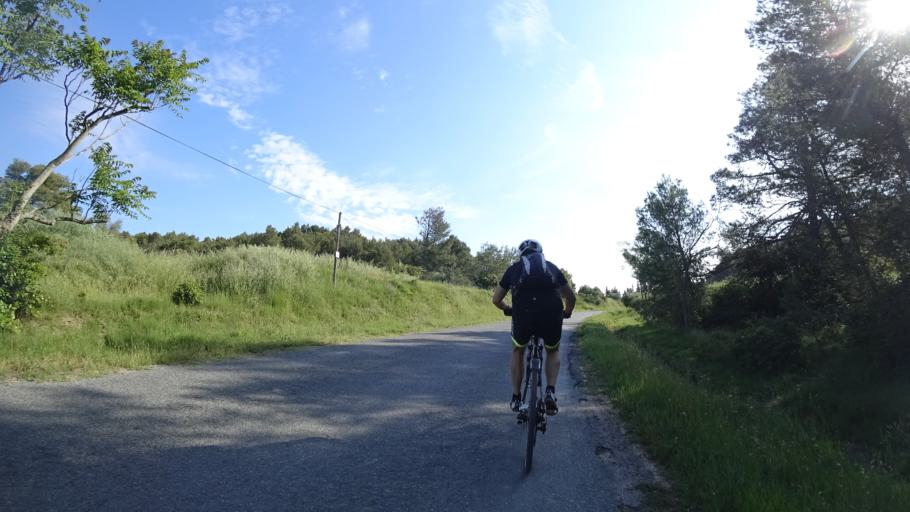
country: FR
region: Languedoc-Roussillon
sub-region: Departement de l'Herault
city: Olonzac
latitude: 43.2450
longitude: 2.7195
